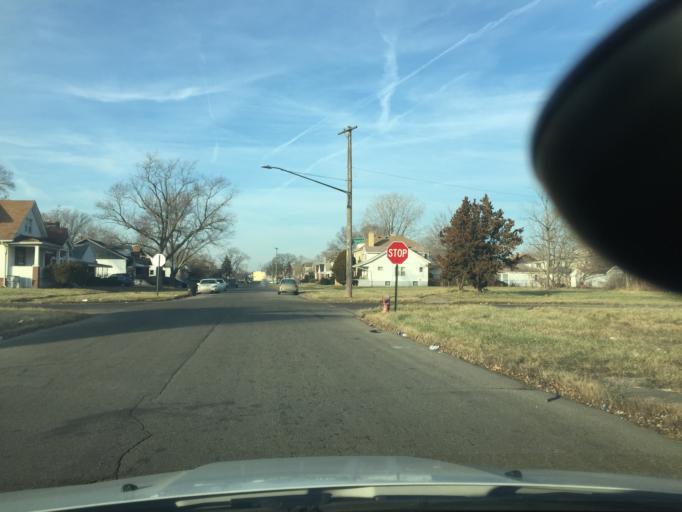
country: US
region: Michigan
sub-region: Macomb County
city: Eastpointe
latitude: 42.4361
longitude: -82.9713
